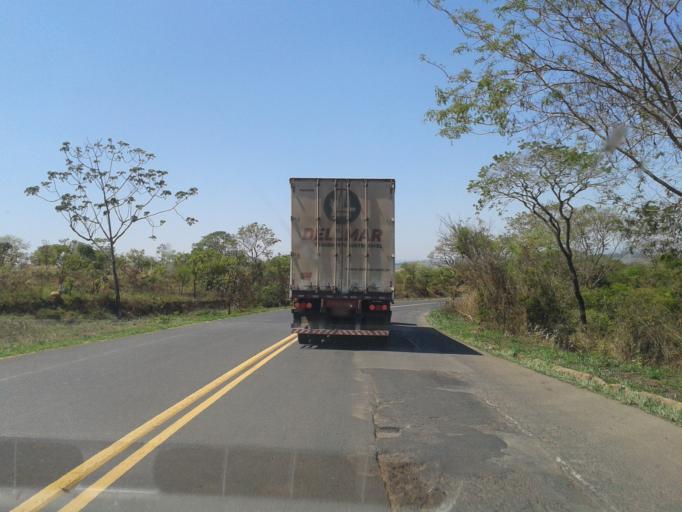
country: BR
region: Minas Gerais
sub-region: Araxa
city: Araxa
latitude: -19.4370
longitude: -47.1951
